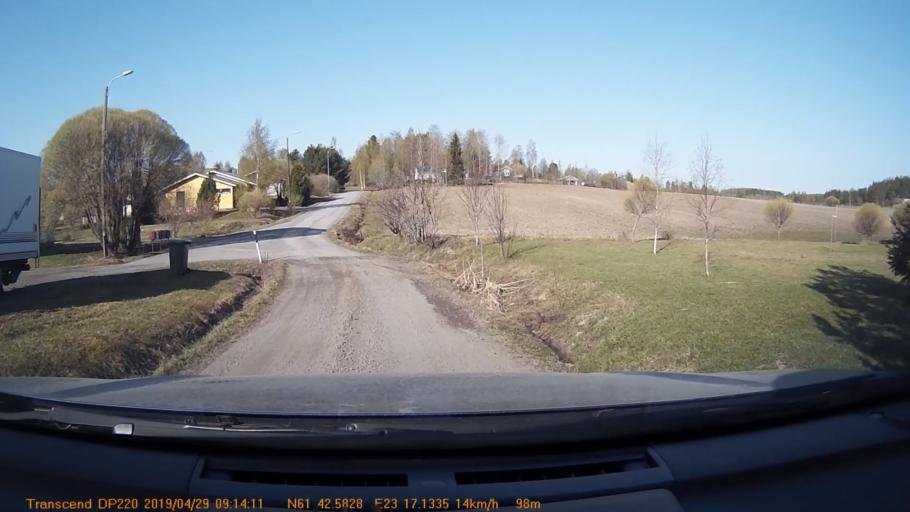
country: FI
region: Pirkanmaa
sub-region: Tampere
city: Viljakkala
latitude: 61.7097
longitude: 23.2856
